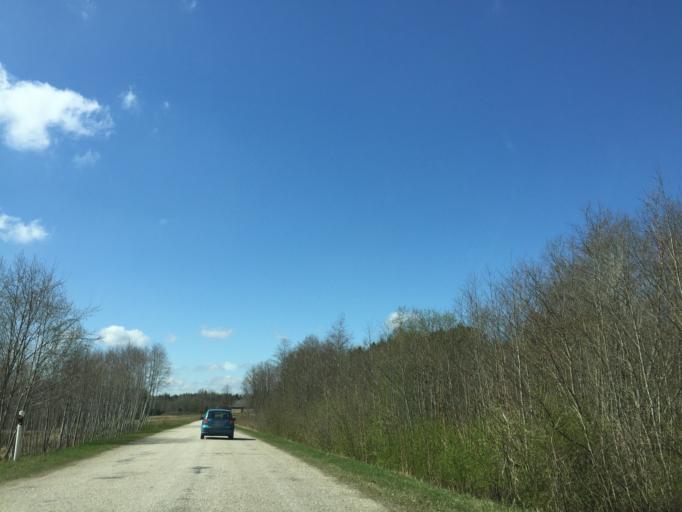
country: EE
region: Tartu
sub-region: Elva linn
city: Elva
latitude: 58.1522
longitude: 26.2304
